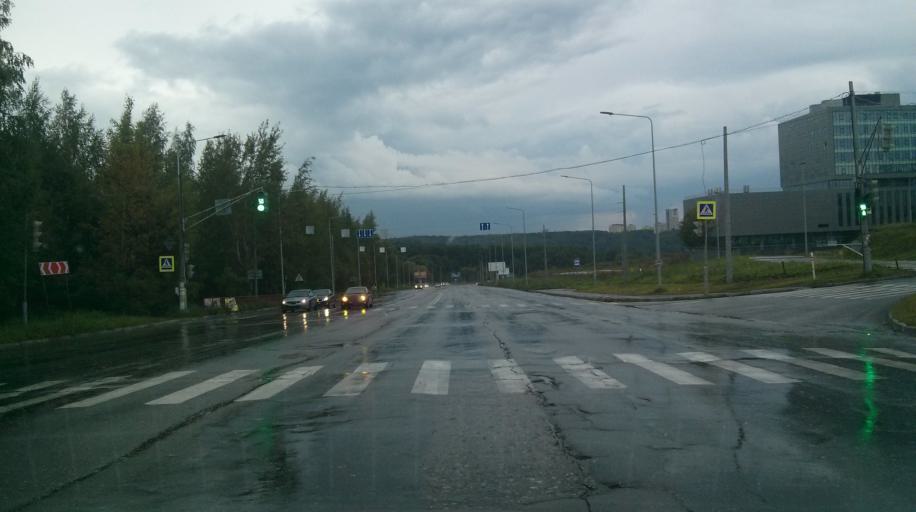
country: RU
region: Nizjnij Novgorod
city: Nizhniy Novgorod
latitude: 56.2662
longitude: 44.0237
